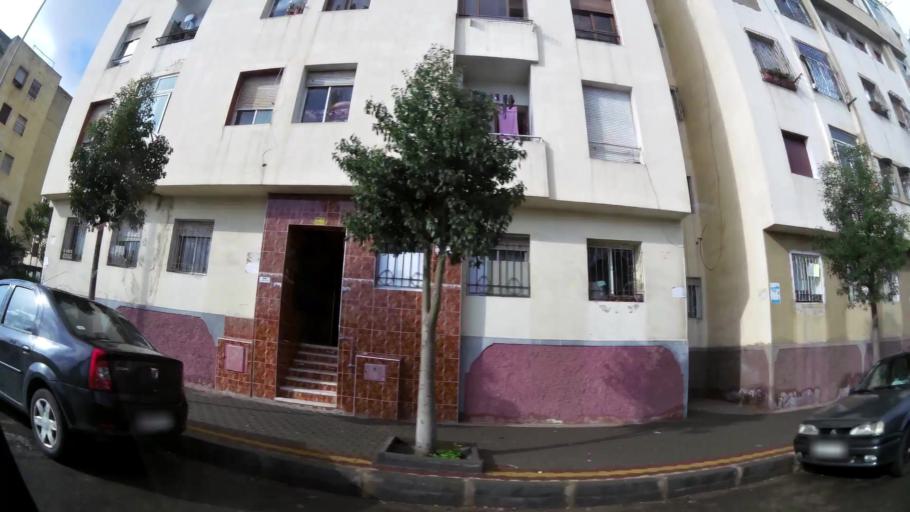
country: MA
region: Grand Casablanca
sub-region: Mediouna
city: Tit Mellil
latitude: 33.5958
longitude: -7.5333
